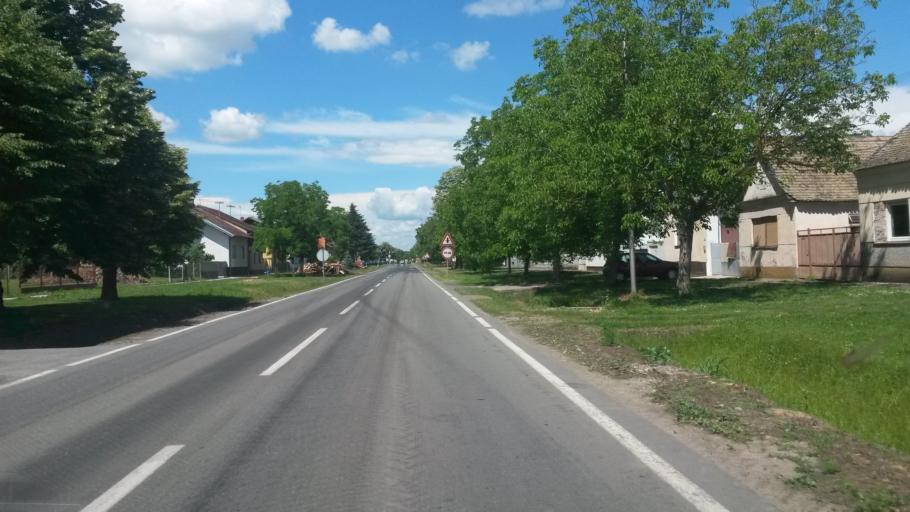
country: HR
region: Osjecko-Baranjska
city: Vuka
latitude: 45.4341
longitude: 18.5046
